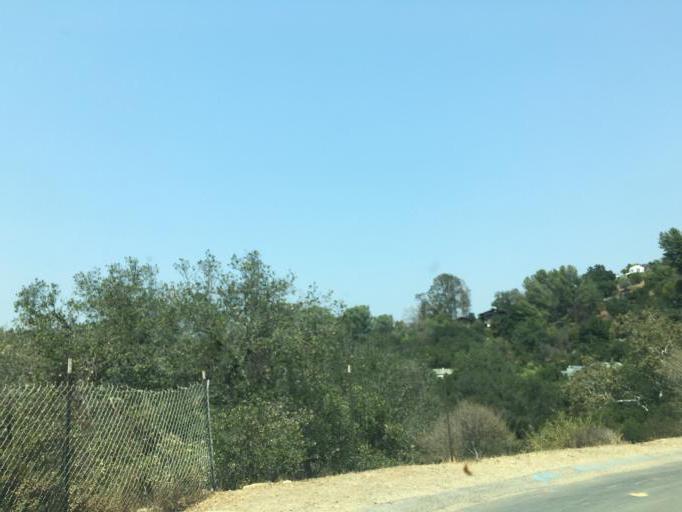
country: US
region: California
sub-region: Los Angeles County
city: Topanga
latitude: 34.1001
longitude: -118.5876
